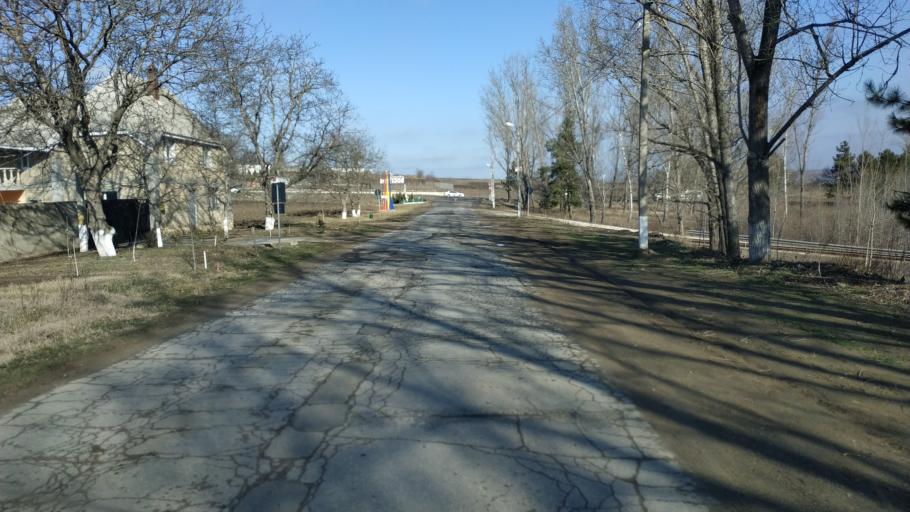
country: MD
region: Laloveni
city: Ialoveni
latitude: 46.9480
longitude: 28.7208
